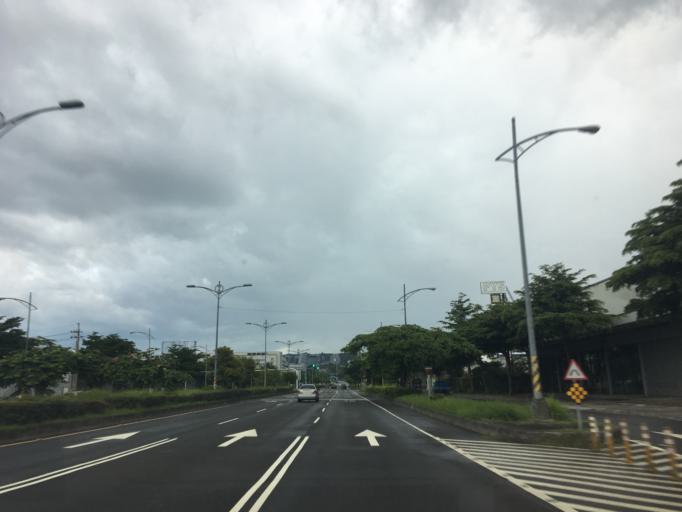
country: TW
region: Taiwan
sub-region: Taichung City
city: Taichung
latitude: 24.2044
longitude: 120.6347
